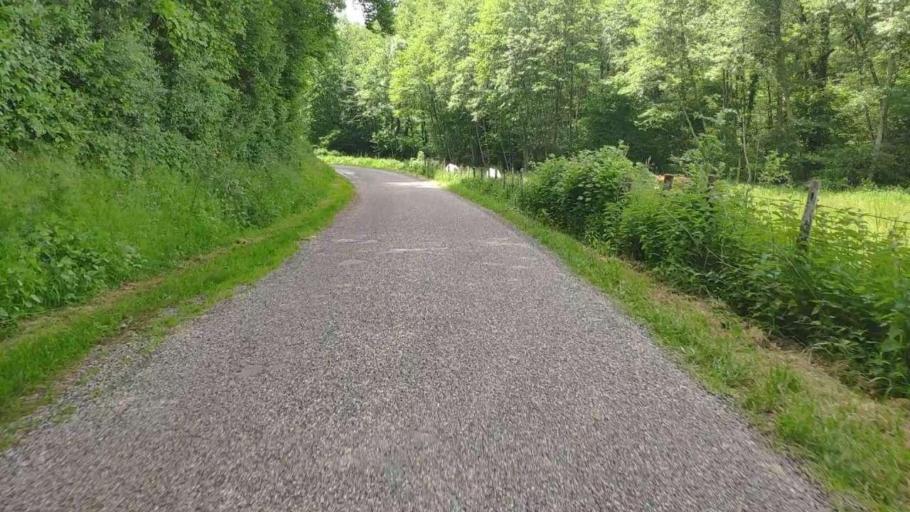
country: FR
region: Franche-Comte
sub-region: Departement du Jura
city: Montmorot
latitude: 46.7436
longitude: 5.5376
